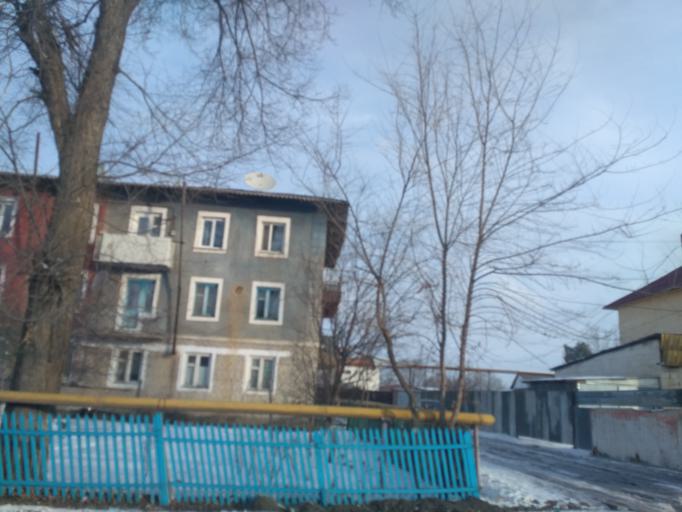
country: KZ
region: Almaty Oblysy
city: Burunday
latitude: 43.2113
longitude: 76.3363
